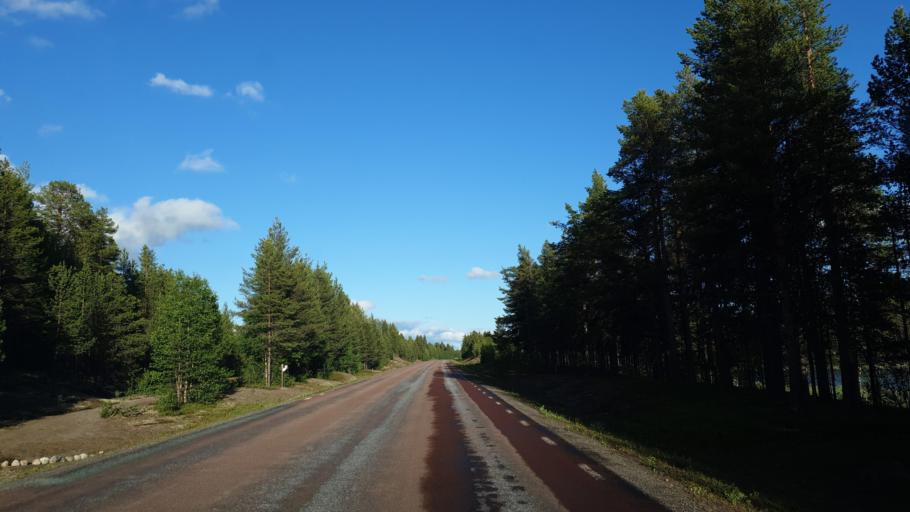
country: SE
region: Norrbotten
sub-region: Arjeplogs Kommun
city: Arjeplog
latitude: 65.9960
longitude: 18.1665
